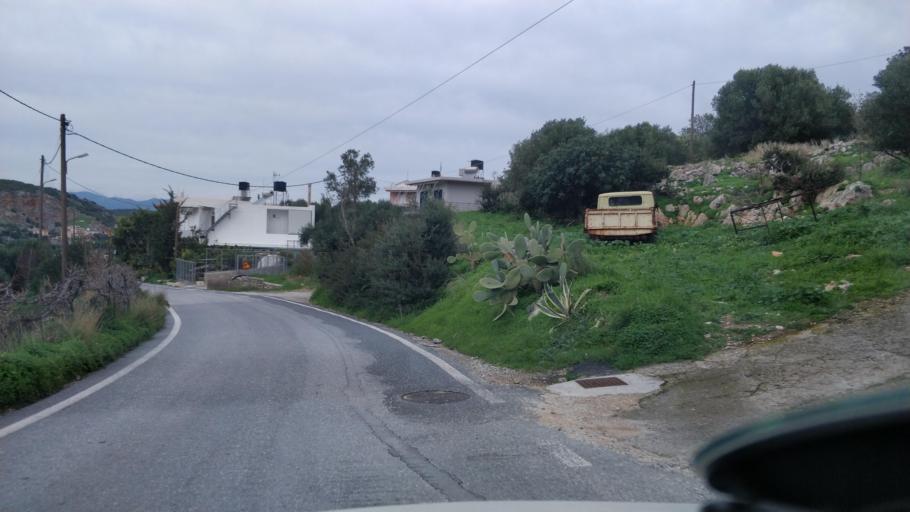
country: GR
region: Crete
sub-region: Nomos Lasithiou
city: Agios Nikolaos
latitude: 35.1191
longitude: 25.7269
